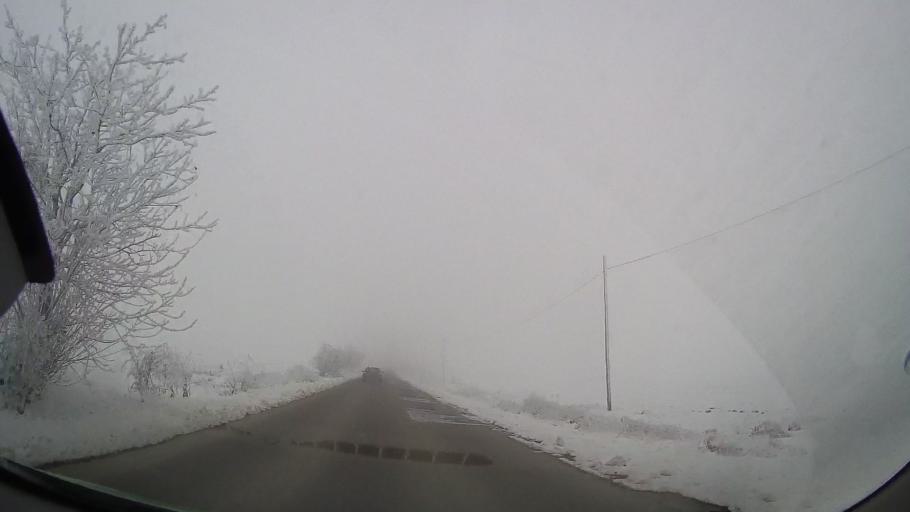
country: RO
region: Neamt
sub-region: Comuna Sabaoani
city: Sabaoani
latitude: 46.9940
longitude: 26.8630
